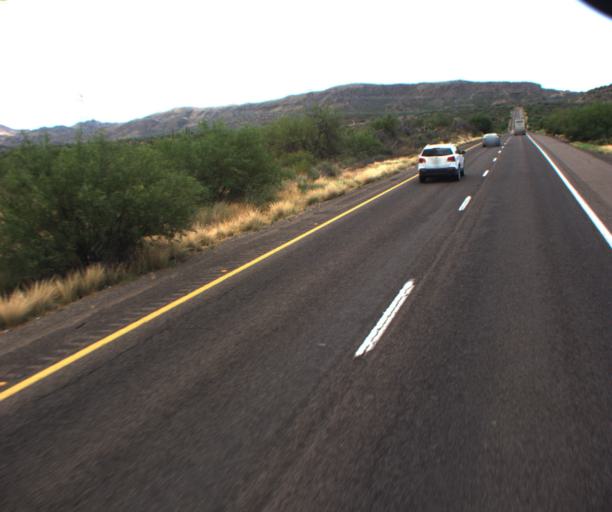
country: US
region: Arizona
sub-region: Yavapai County
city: Black Canyon City
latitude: 34.0075
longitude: -112.1429
